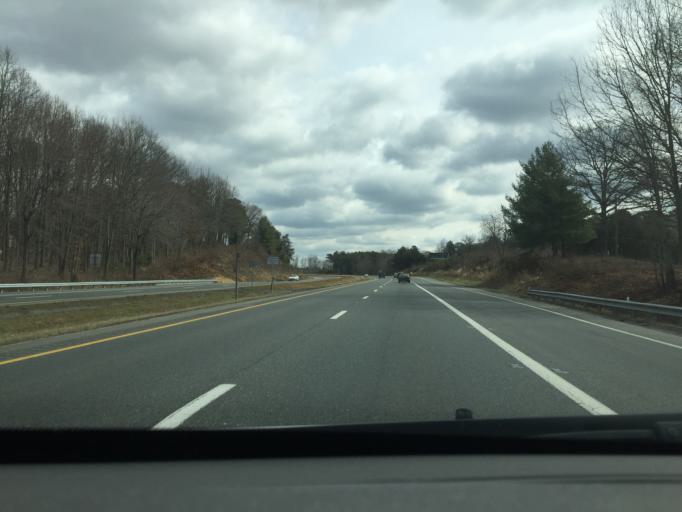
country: US
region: Virginia
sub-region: Campbell County
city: Timberlake
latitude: 37.3124
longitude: -79.2350
